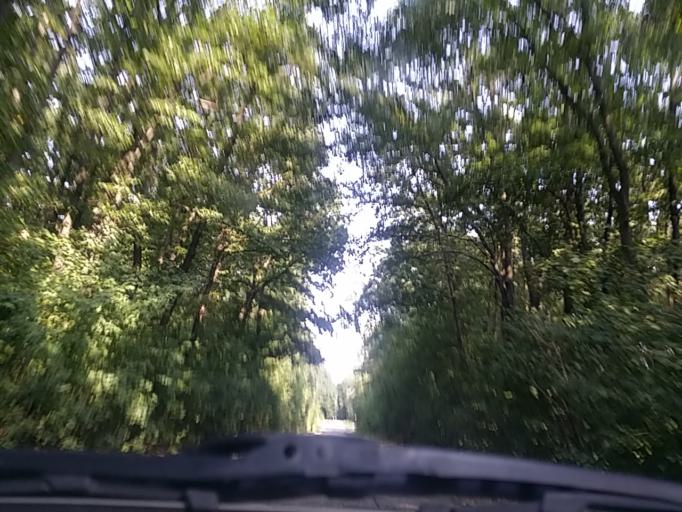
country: HU
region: Komarom-Esztergom
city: Tatabanya
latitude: 47.5301
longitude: 18.3818
